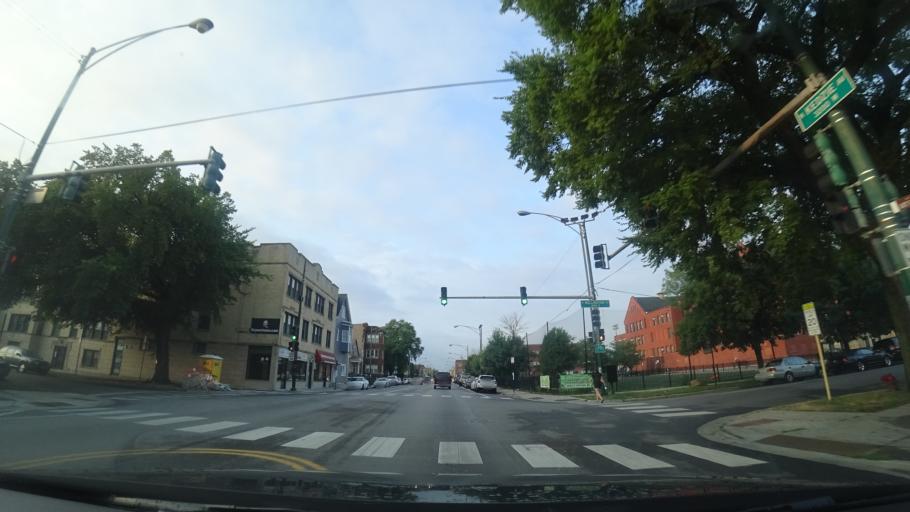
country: US
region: Illinois
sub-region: Cook County
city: Lincolnwood
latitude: 41.9359
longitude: -87.7076
